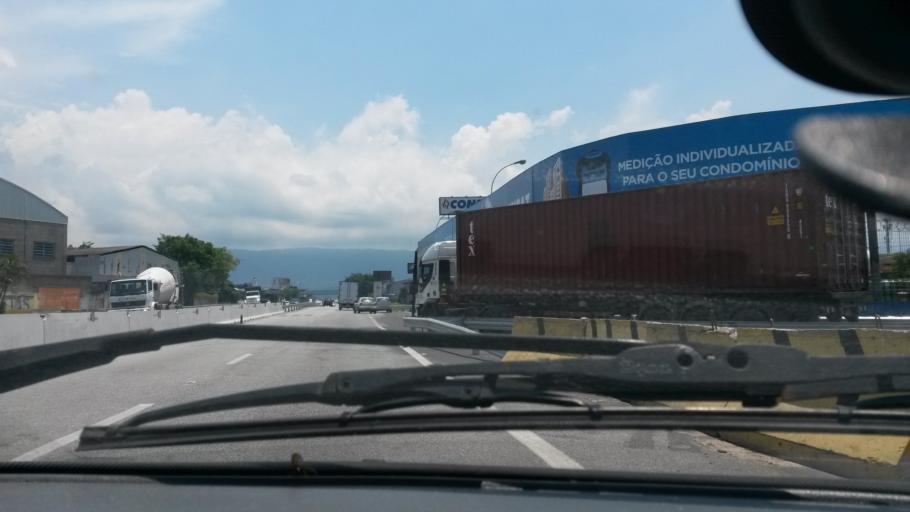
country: BR
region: Sao Paulo
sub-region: Sao Vicente
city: Sao Vicente
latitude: -23.9517
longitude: -46.4120
